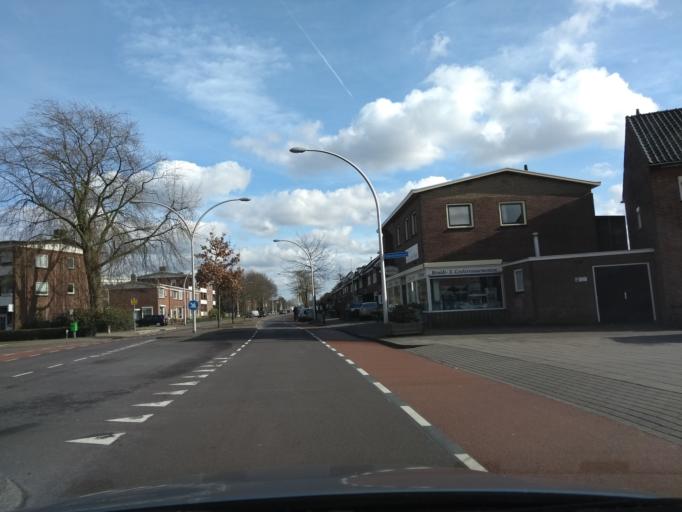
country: NL
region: Overijssel
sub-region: Gemeente Hengelo
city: Hengelo
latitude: 52.2533
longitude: 6.7785
